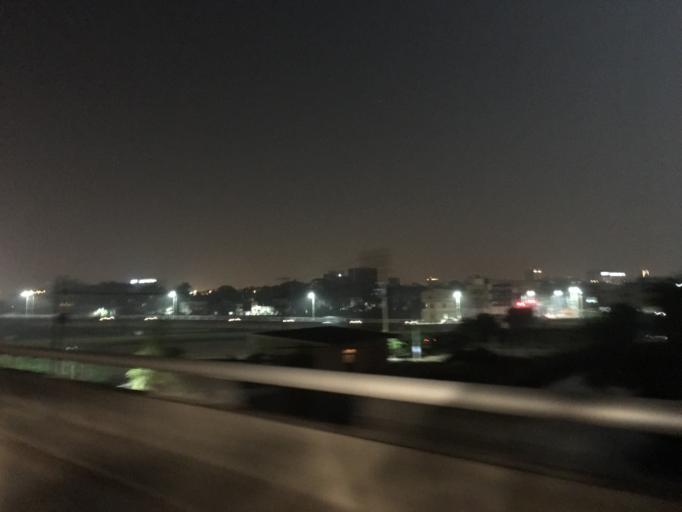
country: TW
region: Taiwan
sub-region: Hsinchu
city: Hsinchu
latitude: 24.6991
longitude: 120.8853
